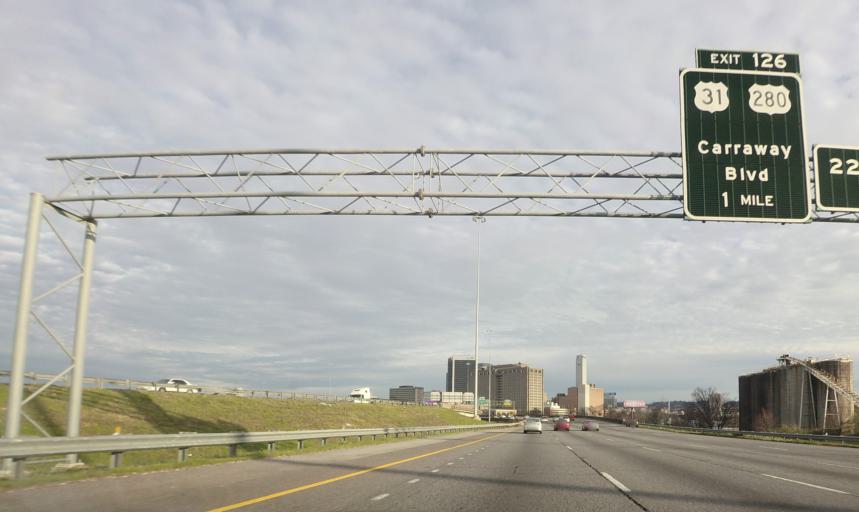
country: US
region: Alabama
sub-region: Jefferson County
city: Birmingham
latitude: 33.5204
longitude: -86.8207
